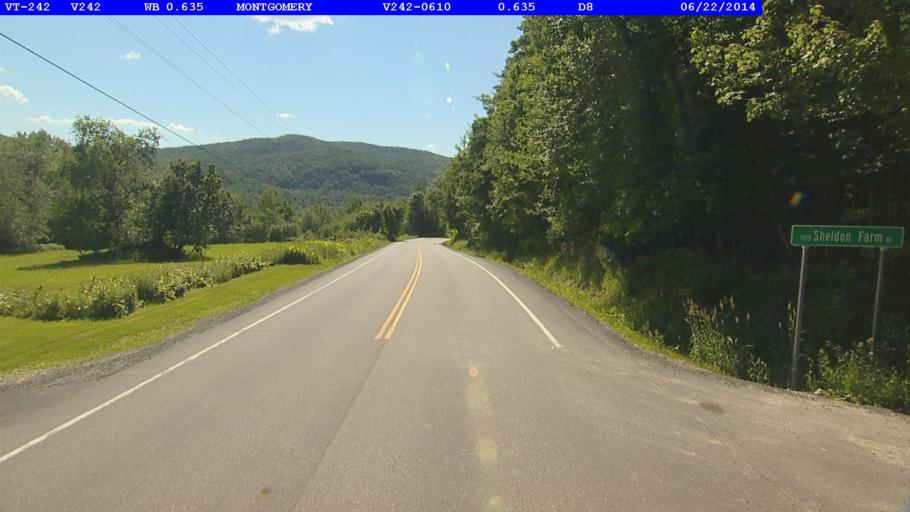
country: US
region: Vermont
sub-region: Franklin County
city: Richford
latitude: 44.8825
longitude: -72.5996
